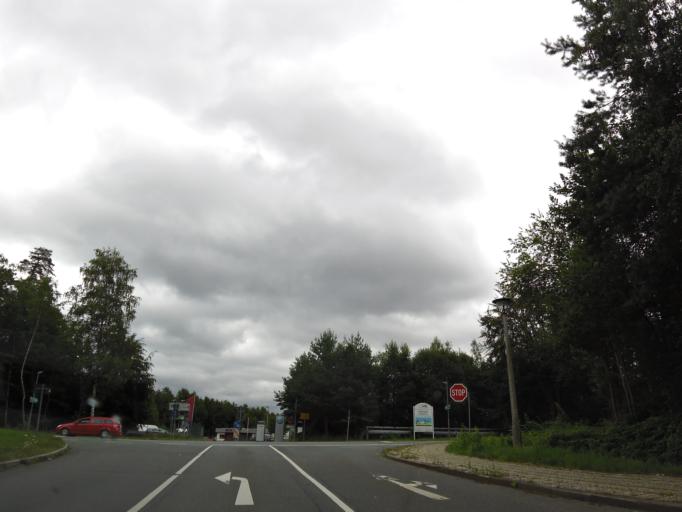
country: DE
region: Thuringia
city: Bad Klosterlausnitz
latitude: 50.9087
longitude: 11.8582
